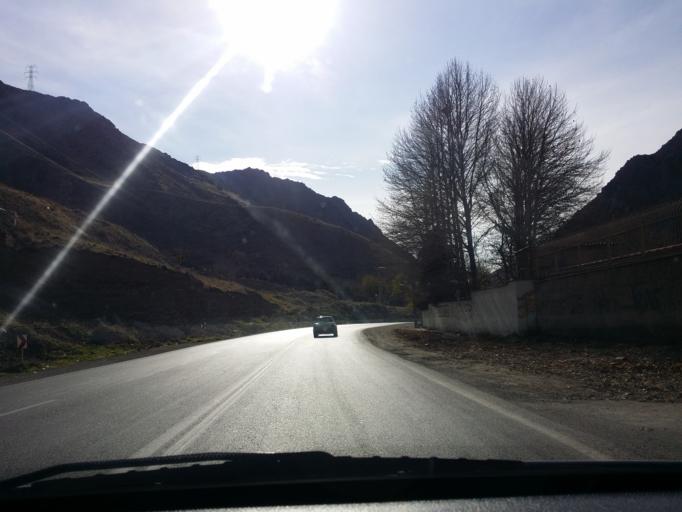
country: IR
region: Alborz
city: Karaj
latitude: 35.9037
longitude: 51.0441
